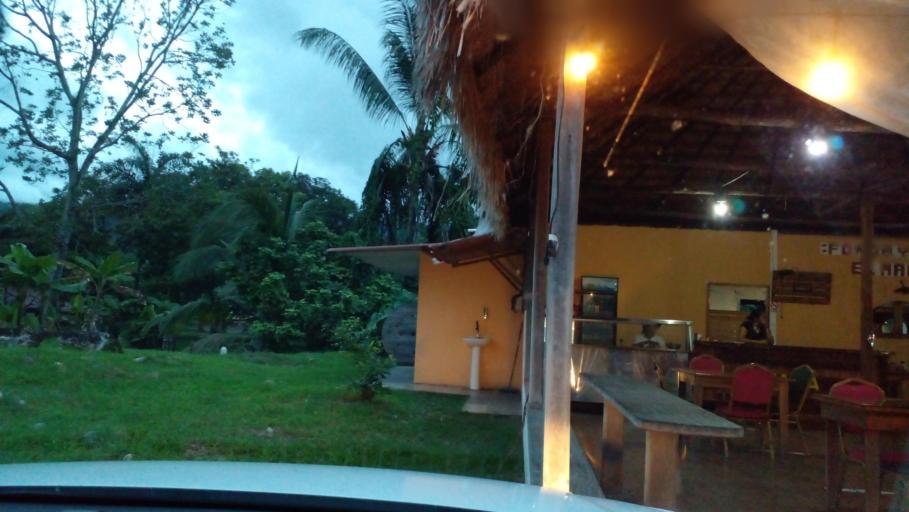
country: PA
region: Bocas del Toro
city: Chiriqui Grande
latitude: 8.9289
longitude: -82.1832
